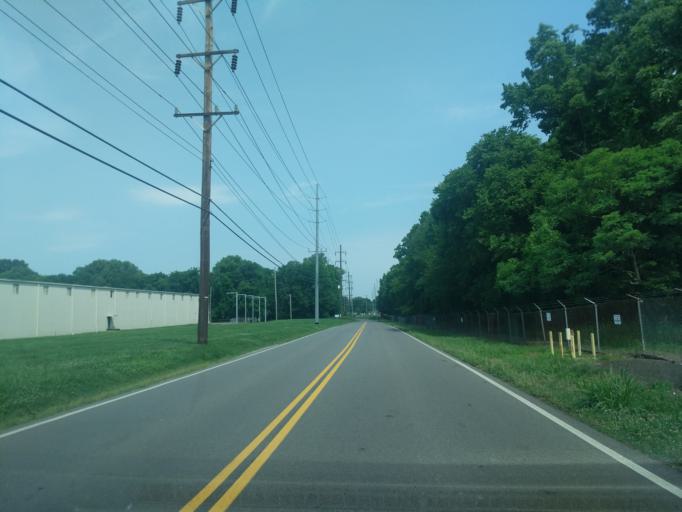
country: US
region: Tennessee
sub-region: Davidson County
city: Lakewood
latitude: 36.2744
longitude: -86.6659
